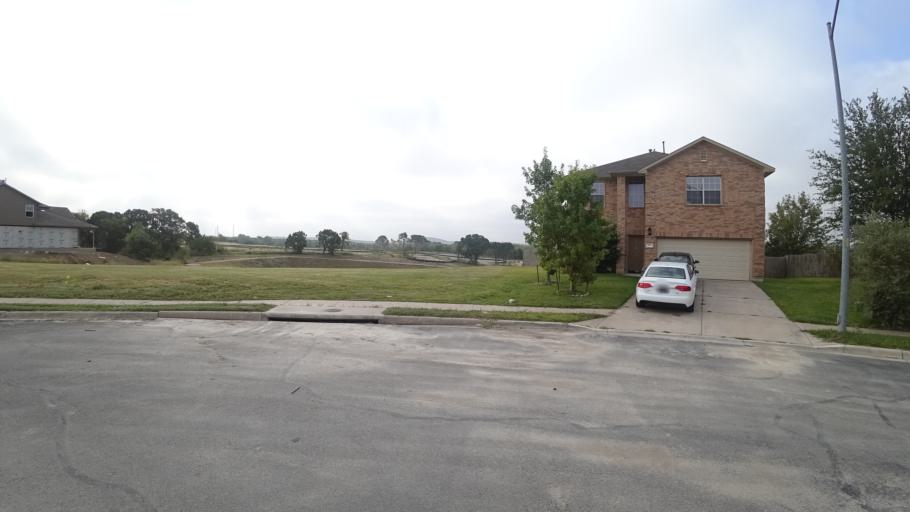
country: US
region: Texas
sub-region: Travis County
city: Pflugerville
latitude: 30.3560
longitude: -97.6452
